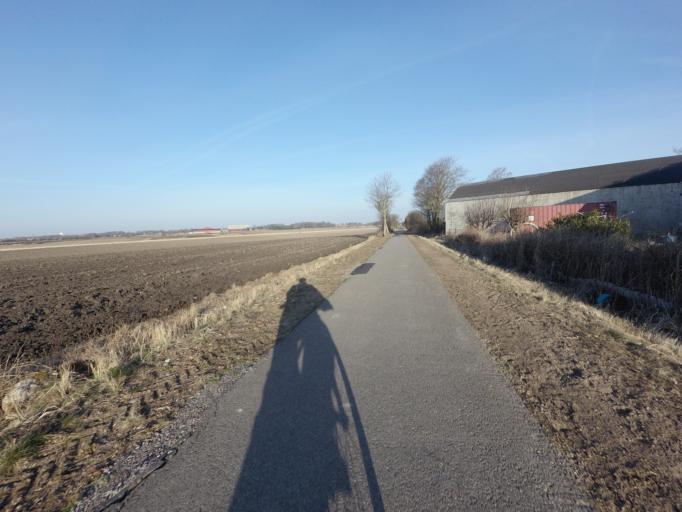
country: SE
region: Skane
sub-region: Hoganas Kommun
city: Hoganas
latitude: 56.1955
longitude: 12.6014
